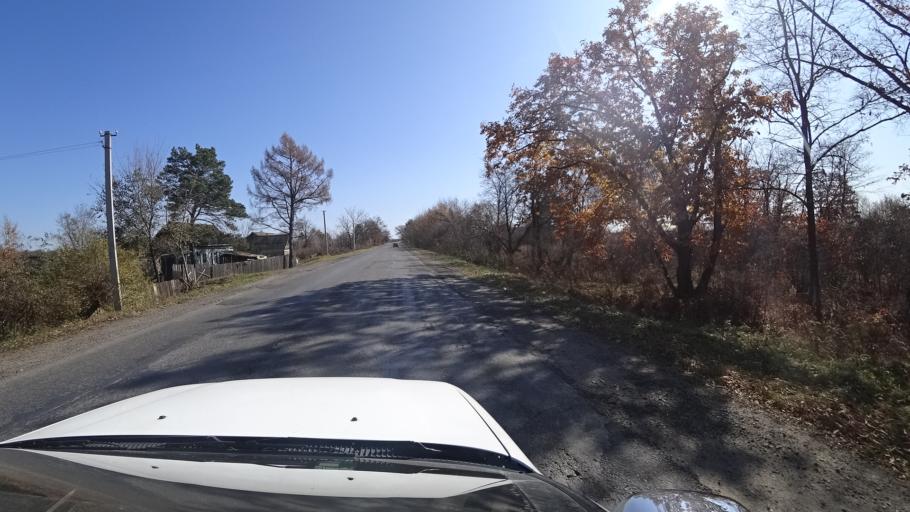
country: RU
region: Primorskiy
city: Dal'nerechensk
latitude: 45.9165
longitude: 133.7833
